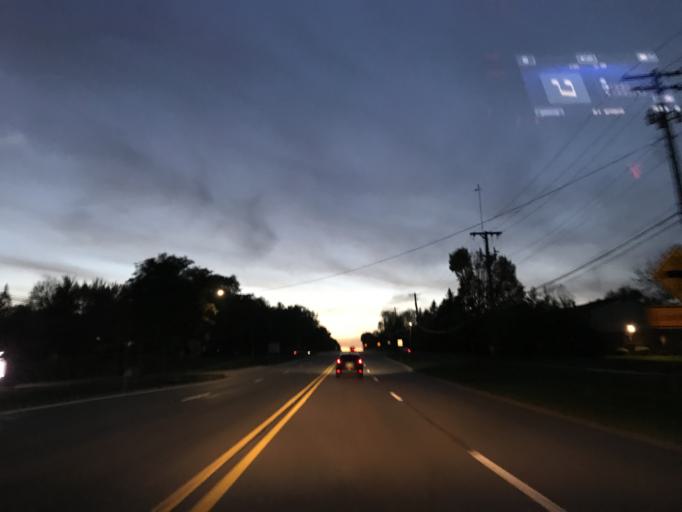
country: US
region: Michigan
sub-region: Wayne County
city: Northville
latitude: 42.4371
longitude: -83.4932
